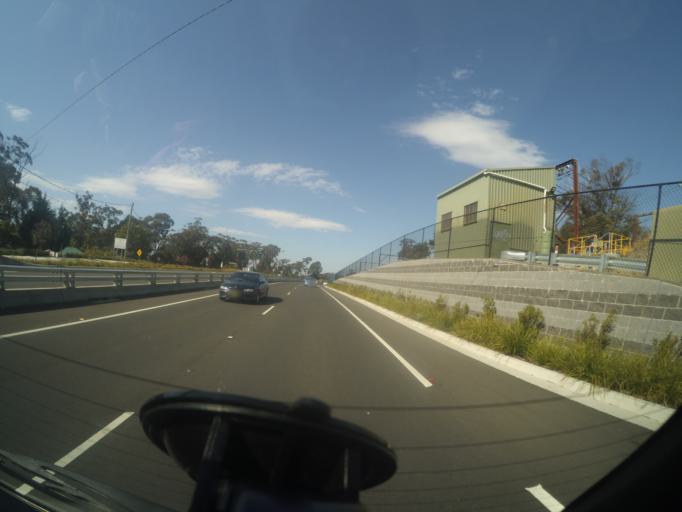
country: AU
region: New South Wales
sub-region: Blue Mountains Municipality
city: Hazelbrook
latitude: -33.7300
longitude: 150.4618
